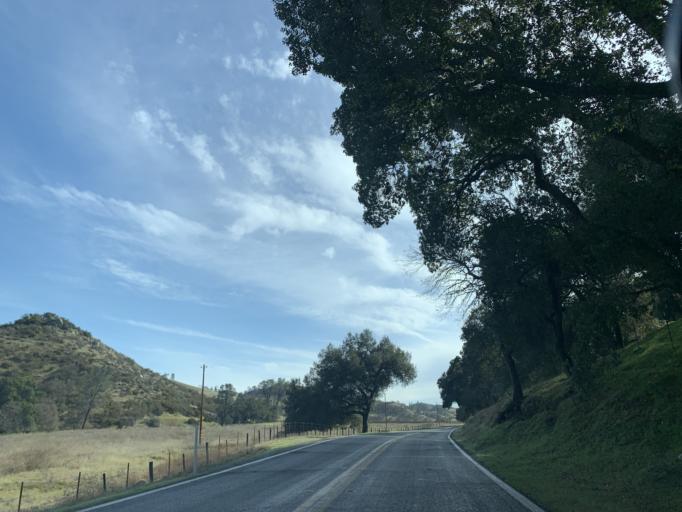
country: US
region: California
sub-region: Monterey County
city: Soledad
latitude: 36.5169
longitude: -121.1260
